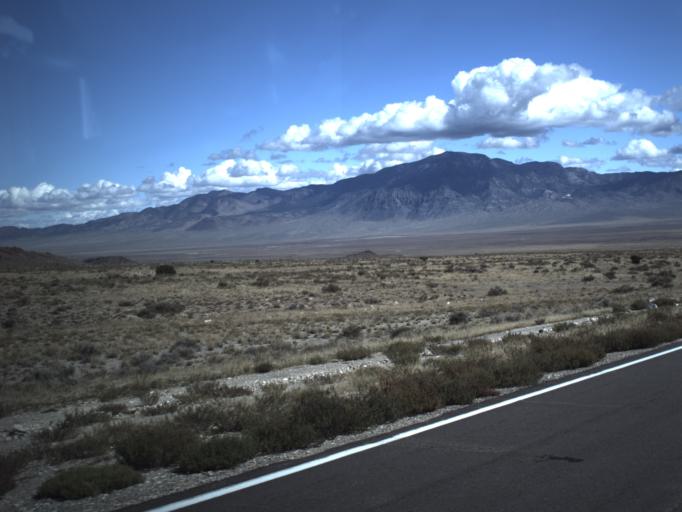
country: US
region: Utah
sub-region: Beaver County
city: Milford
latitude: 38.4983
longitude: -113.4925
